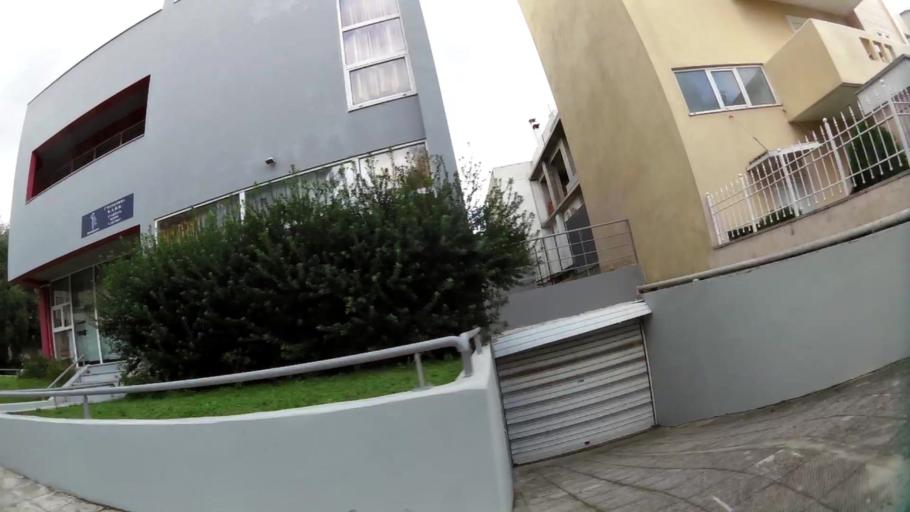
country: GR
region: Attica
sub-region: Nomarchia Athinas
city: Melissia
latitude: 38.0553
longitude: 23.8227
